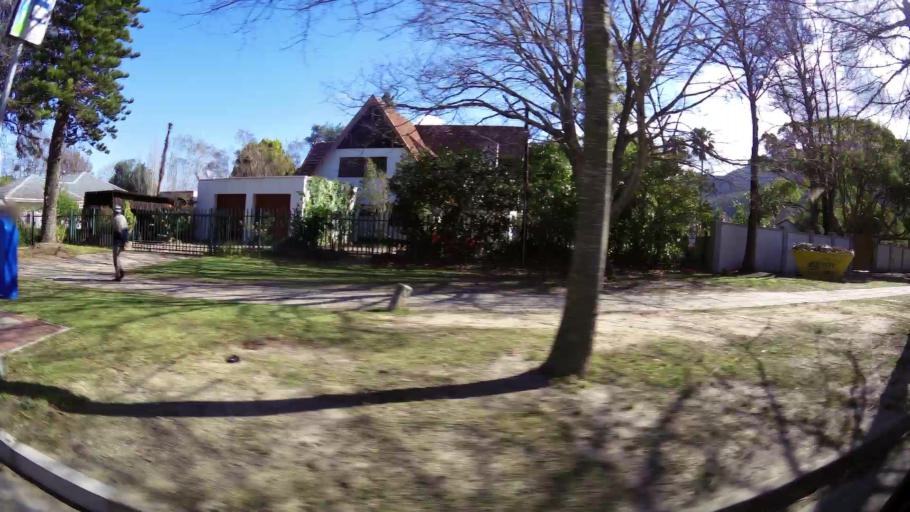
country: ZA
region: Western Cape
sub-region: Eden District Municipality
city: George
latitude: -33.9488
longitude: 22.4630
